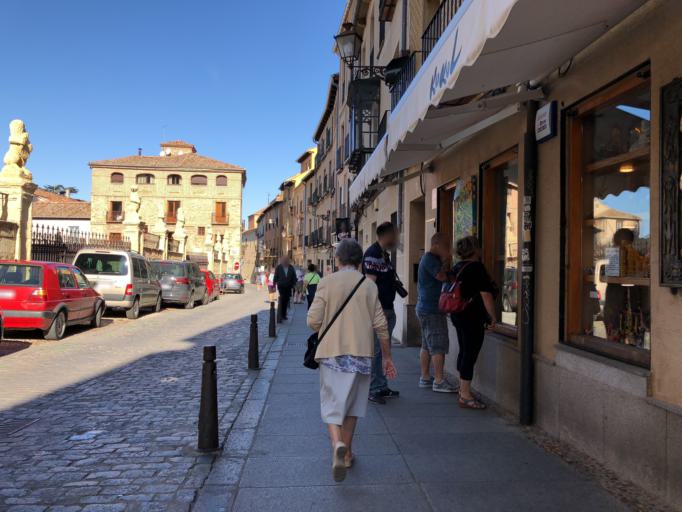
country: ES
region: Castille and Leon
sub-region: Provincia de Segovia
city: Segovia
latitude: 40.9507
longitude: -4.1256
